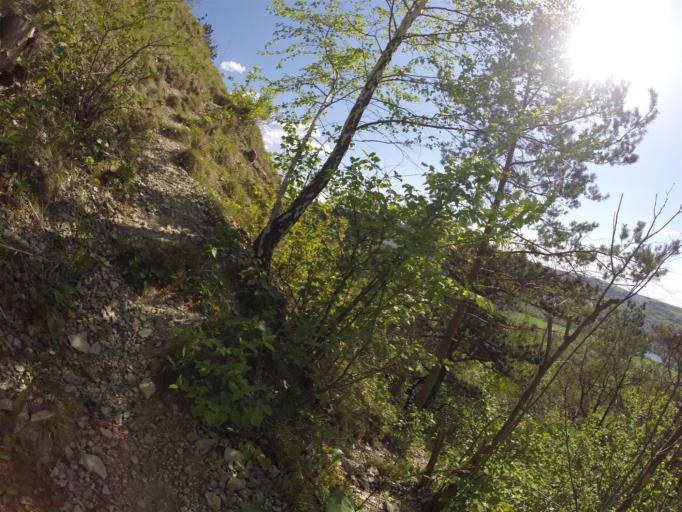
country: DE
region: Thuringia
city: Jena
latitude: 50.9132
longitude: 11.5946
